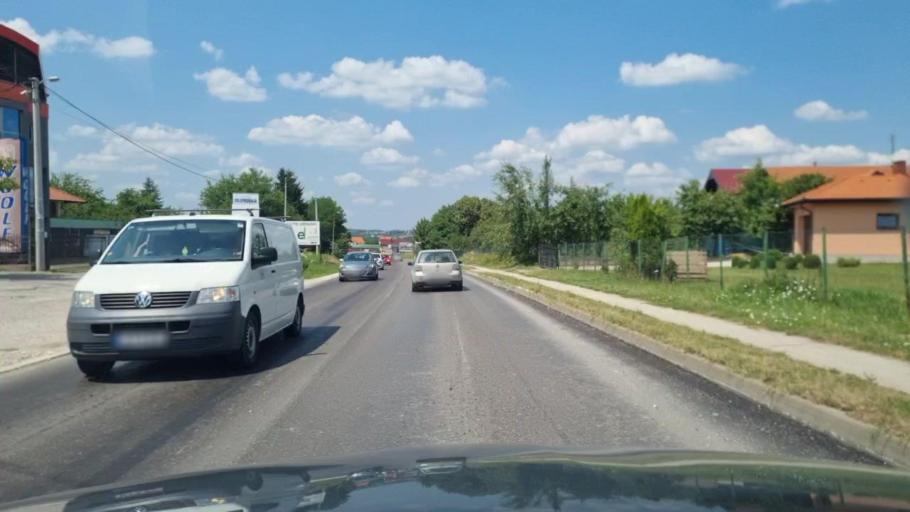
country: BA
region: Federation of Bosnia and Herzegovina
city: Srebrenik
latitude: 44.7166
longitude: 18.4899
